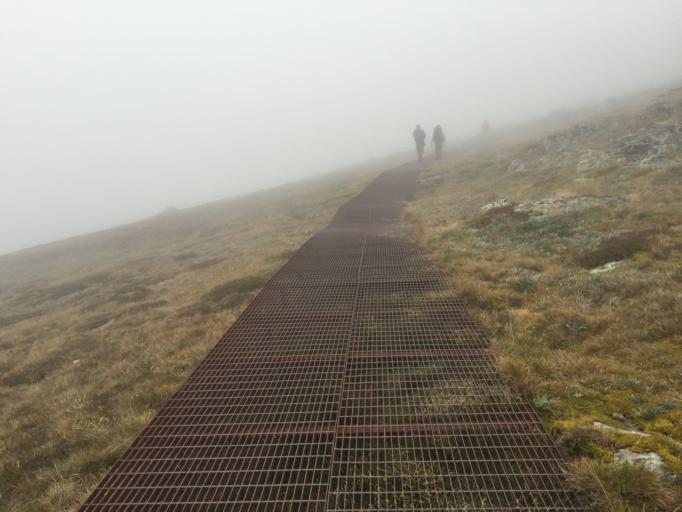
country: AU
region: New South Wales
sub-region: Snowy River
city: Jindabyne
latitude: -36.4633
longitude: 148.2699
